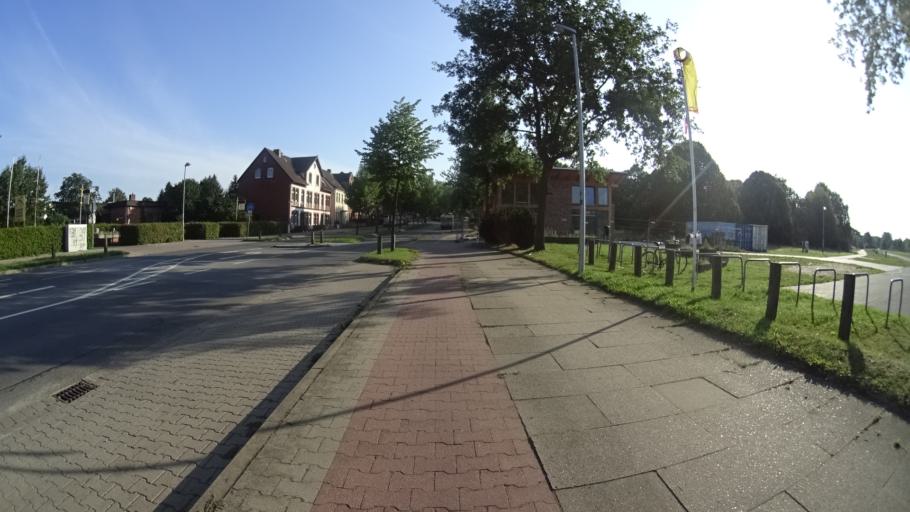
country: DE
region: Lower Saxony
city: Lueneburg
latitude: 53.2473
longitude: 10.3922
